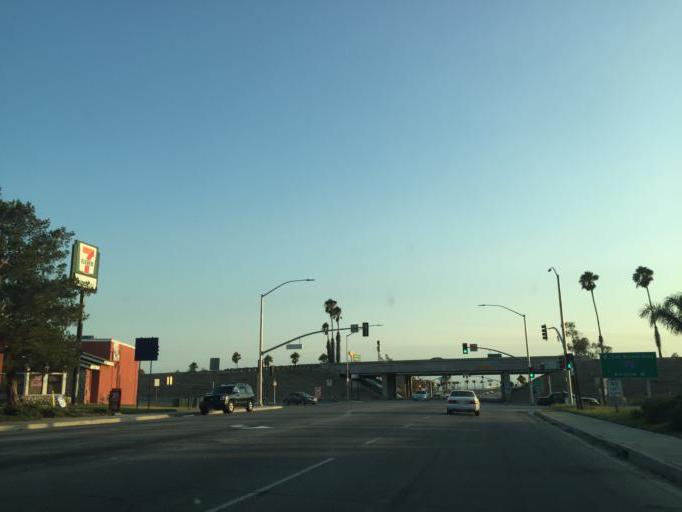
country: US
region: California
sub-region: San Bernardino County
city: Muscoy
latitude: 34.1921
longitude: -117.3609
